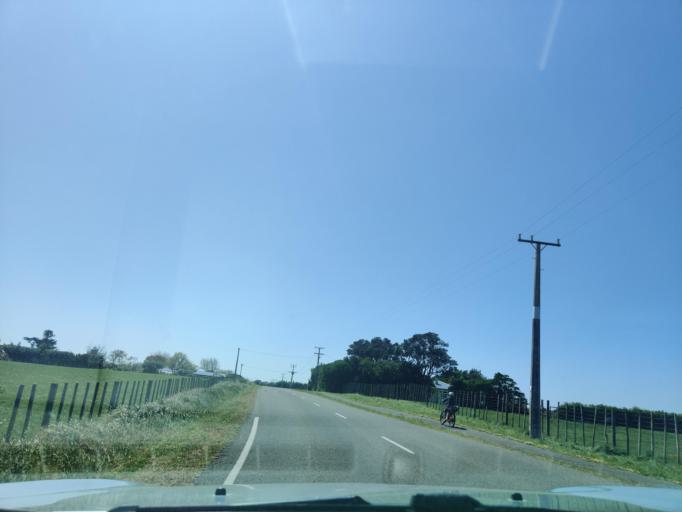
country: NZ
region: Taranaki
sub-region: South Taranaki District
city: Hawera
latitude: -39.5971
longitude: 174.2668
